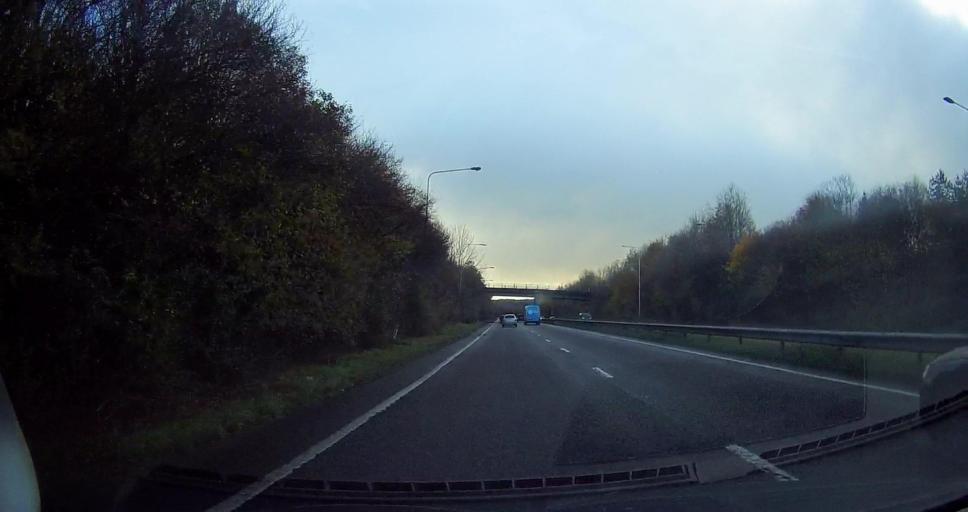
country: GB
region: England
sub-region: West Sussex
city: Hurstpierpoint
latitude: 50.9556
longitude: -0.1933
